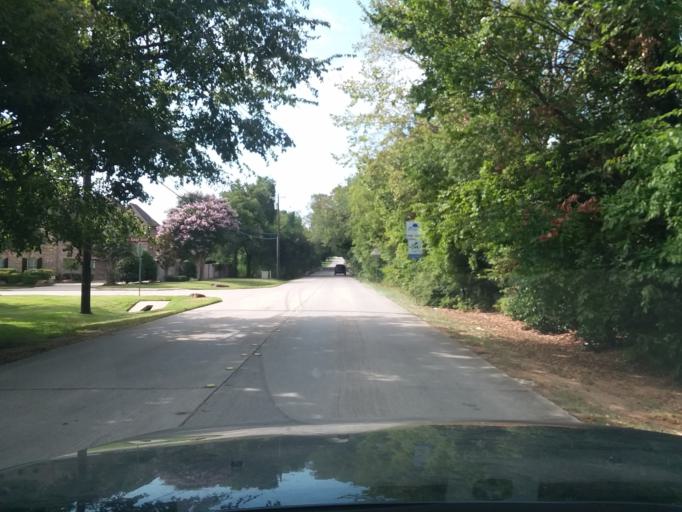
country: US
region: Texas
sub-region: Denton County
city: Double Oak
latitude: 33.0581
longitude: -97.1097
